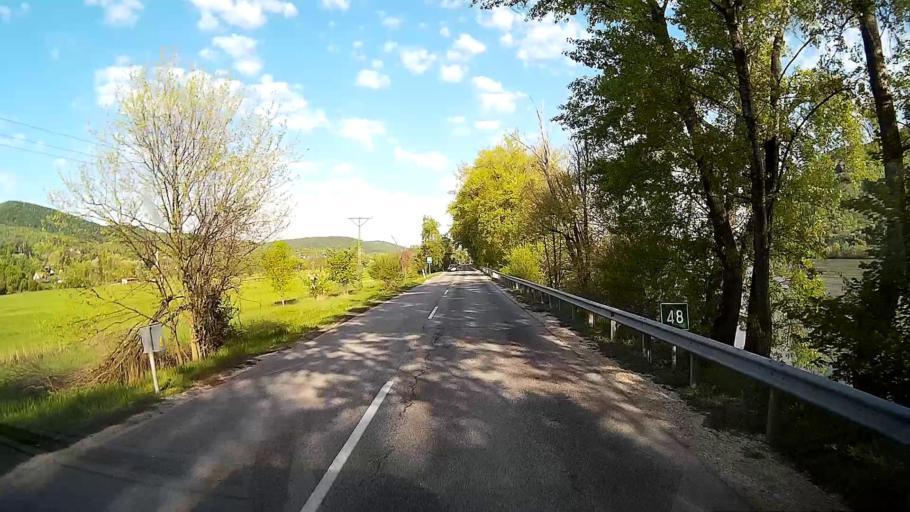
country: HU
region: Pest
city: Nagymaros
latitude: 47.7631
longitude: 18.9233
